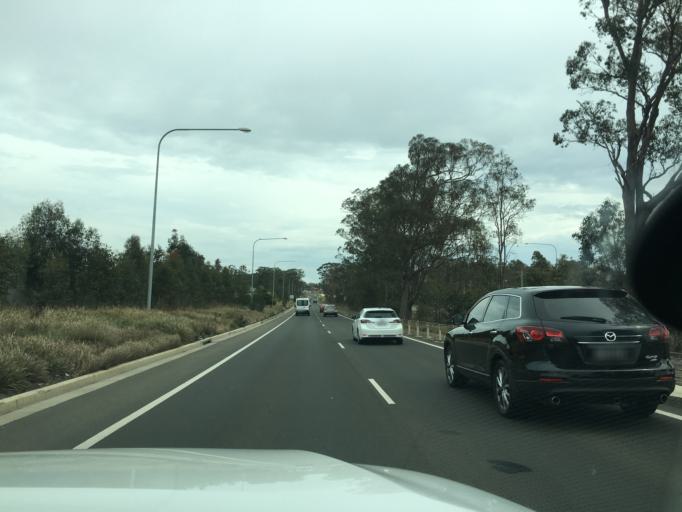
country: AU
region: New South Wales
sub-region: Campbelltown Municipality
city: Denham Court
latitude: -33.9786
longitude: 150.8060
